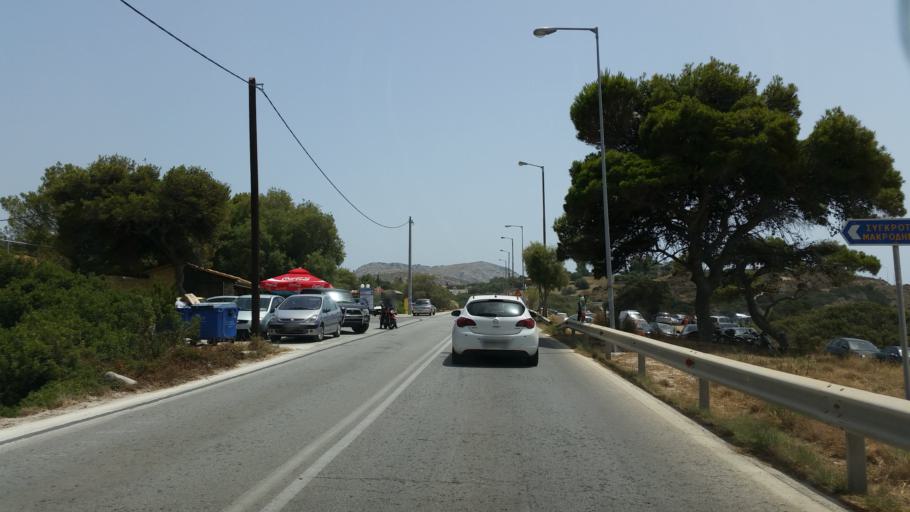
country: GR
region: Attica
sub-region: Nomarchia Anatolikis Attikis
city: Palaia Fokaia
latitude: 37.7031
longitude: 23.9400
